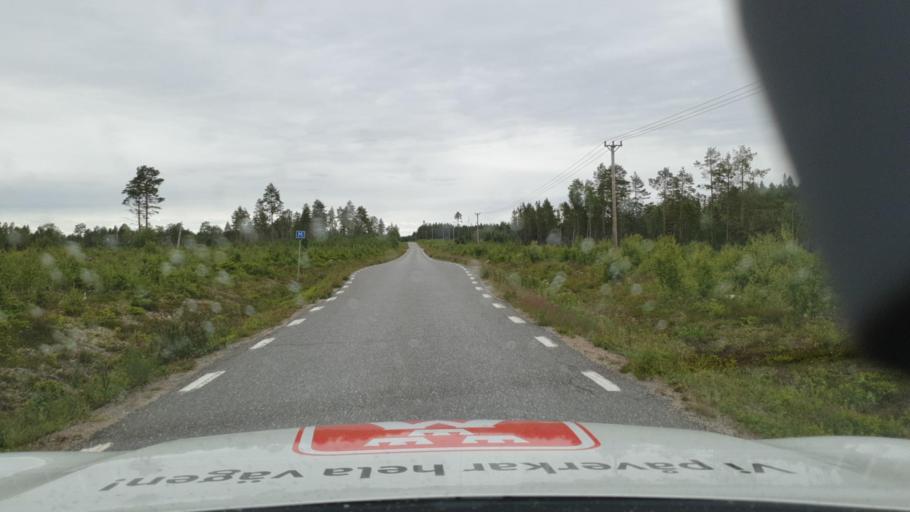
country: SE
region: Vaesterbotten
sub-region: Nordmalings Kommun
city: Nordmaling
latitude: 63.4478
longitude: 19.4681
